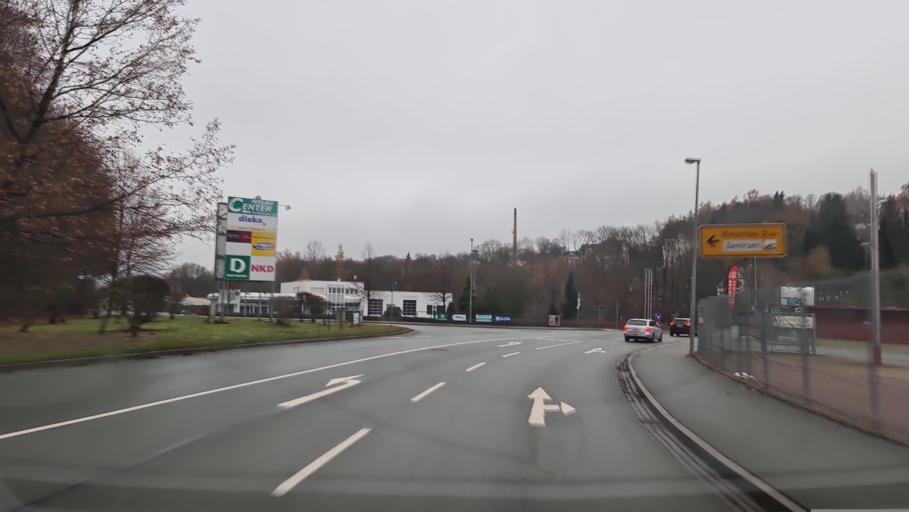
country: DE
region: Saxony
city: Mylau
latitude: 50.6183
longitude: 12.2754
